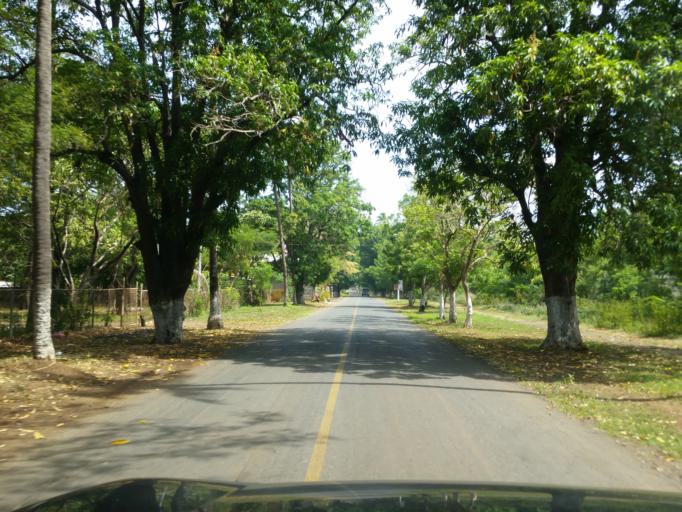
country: NI
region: Managua
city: Masachapa
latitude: 11.7951
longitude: -86.5158
